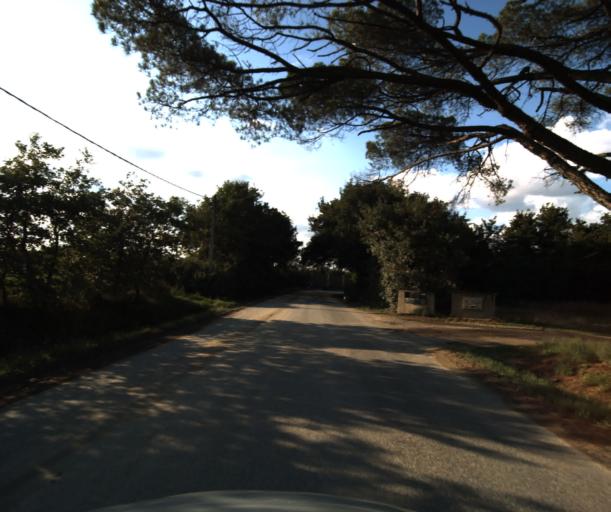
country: FR
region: Midi-Pyrenees
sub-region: Departement de la Haute-Garonne
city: Seysses
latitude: 43.4778
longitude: 1.3241
